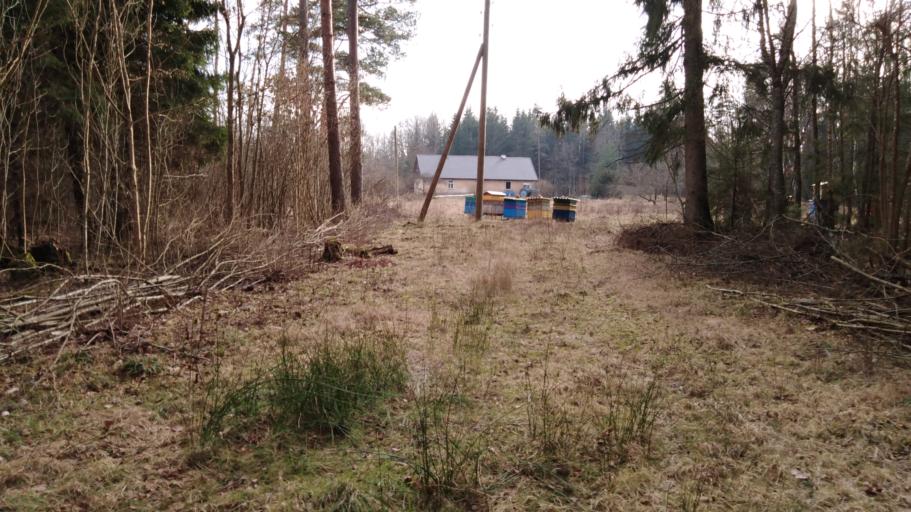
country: LV
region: Kuldigas Rajons
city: Kuldiga
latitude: 57.0373
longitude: 21.8557
